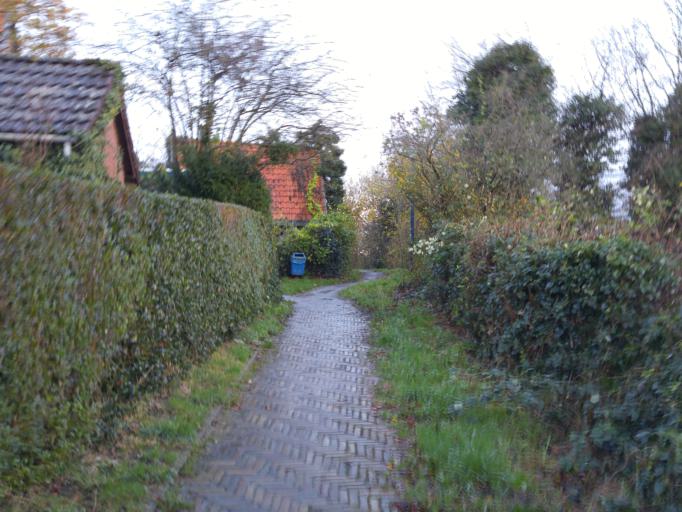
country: NL
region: Gelderland
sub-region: Gemeente Wageningen
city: Wageningen
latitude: 51.9655
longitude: 5.6732
